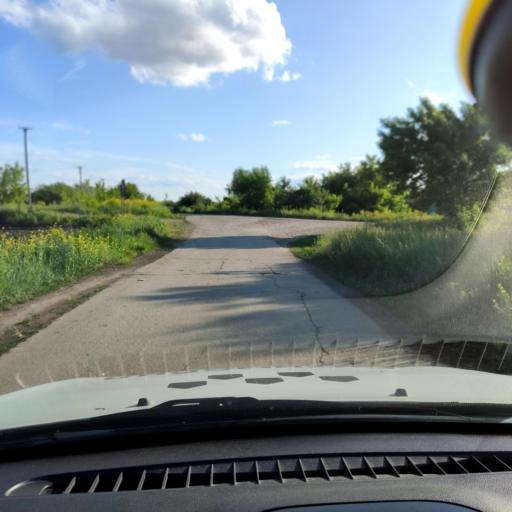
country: RU
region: Samara
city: Tol'yatti
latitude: 53.5920
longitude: 49.4537
